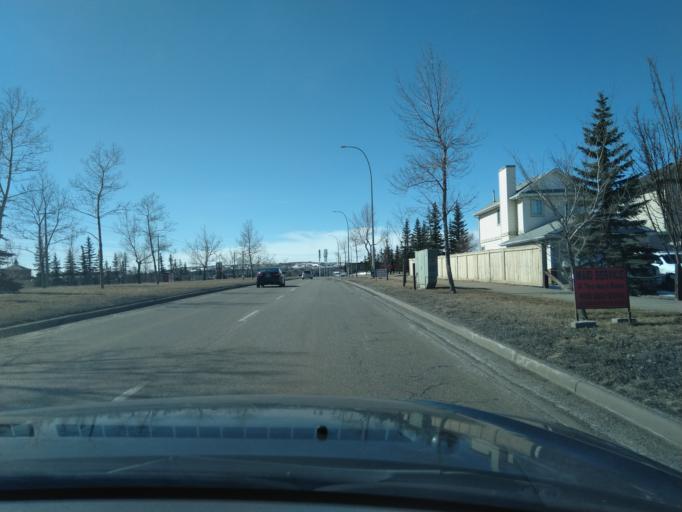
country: CA
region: Alberta
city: Calgary
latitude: 51.1443
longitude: -114.0669
